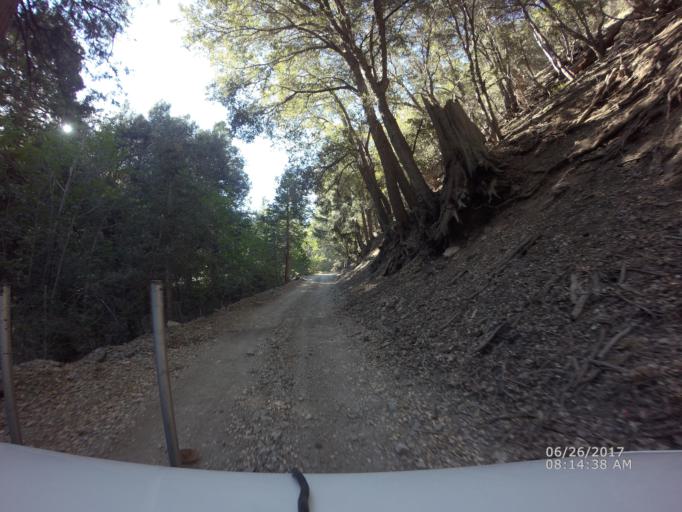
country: US
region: California
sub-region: San Bernardino County
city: Pinon Hills
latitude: 34.3813
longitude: -117.7676
